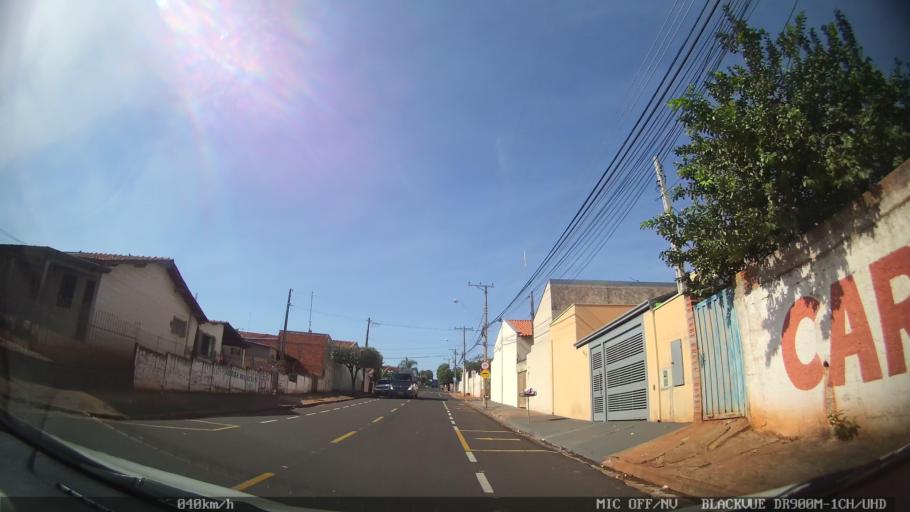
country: BR
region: Sao Paulo
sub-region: Sao Jose Do Rio Preto
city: Sao Jose do Rio Preto
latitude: -20.7950
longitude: -49.4222
